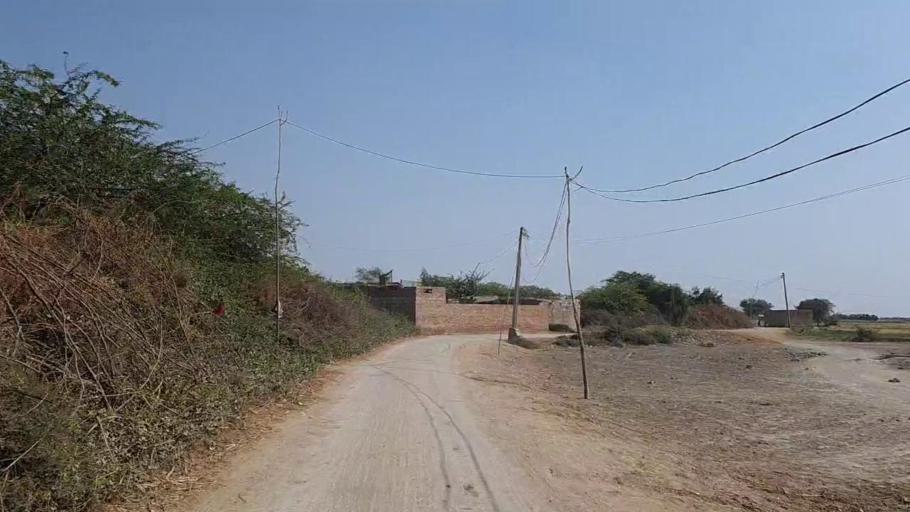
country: PK
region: Sindh
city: Daro Mehar
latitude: 24.7914
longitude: 68.1780
